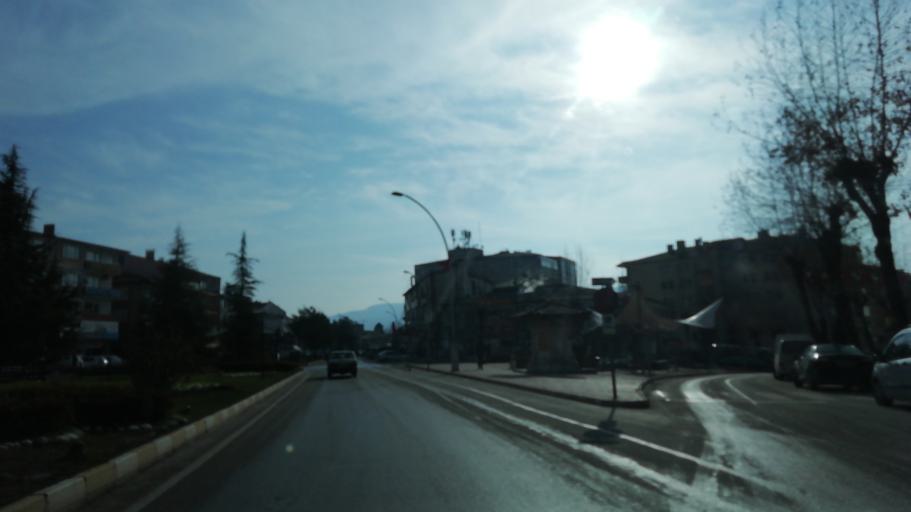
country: TR
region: Karabuk
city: Safranbolu
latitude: 41.2509
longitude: 32.6815
